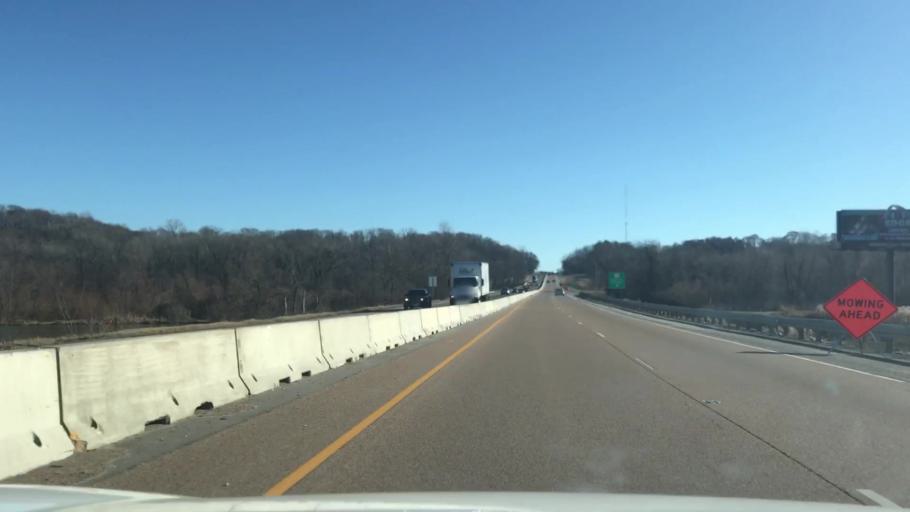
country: US
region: Illinois
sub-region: Saint Clair County
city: Alorton
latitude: 38.5710
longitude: -90.0952
